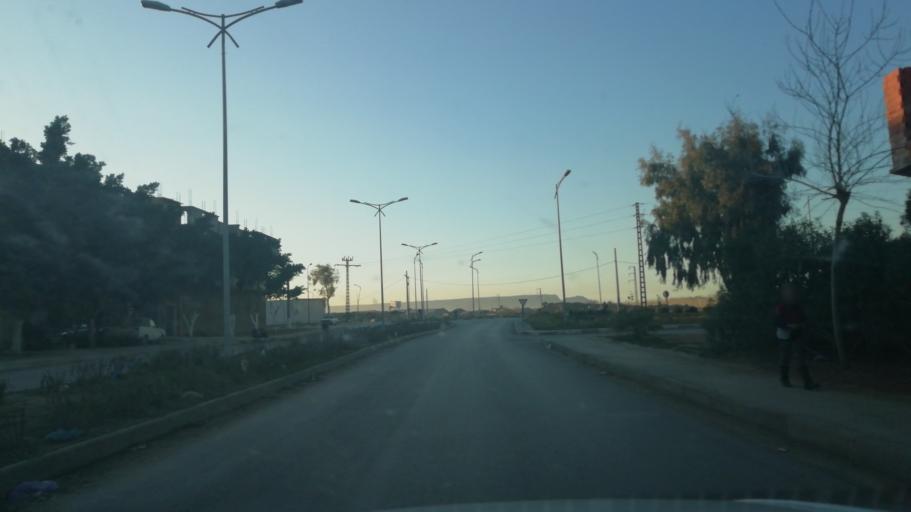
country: DZ
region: Oran
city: Es Senia
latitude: 35.6511
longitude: -0.5788
